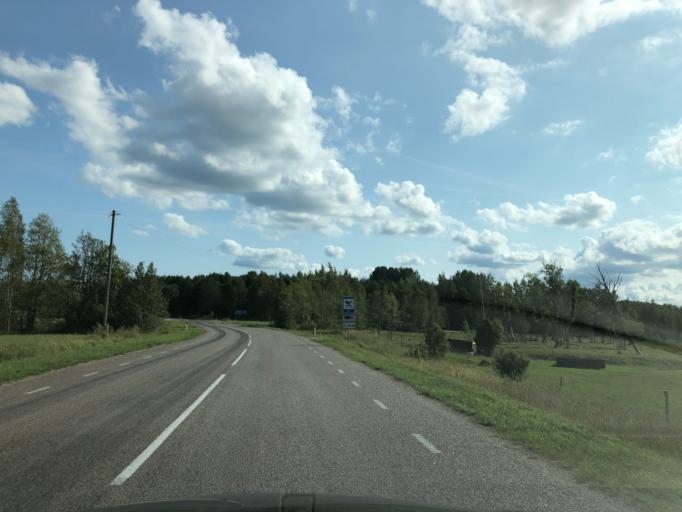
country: EE
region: Hiiumaa
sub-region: Kaerdla linn
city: Kardla
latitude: 58.7207
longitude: 22.5633
